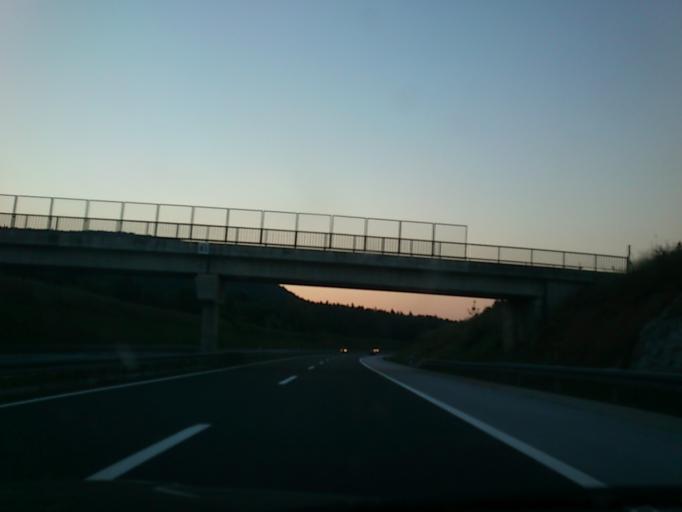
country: HR
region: Karlovacka
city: Ostarije
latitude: 45.1933
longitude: 15.2665
